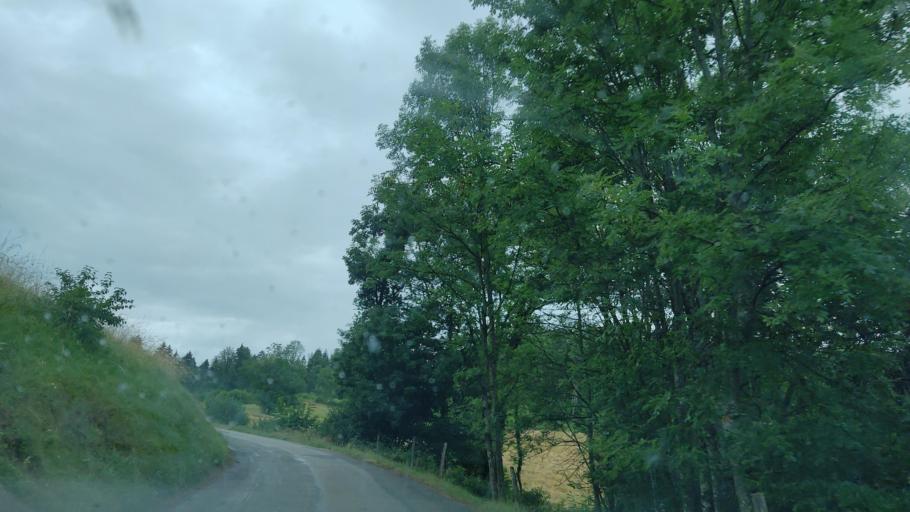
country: FR
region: Rhone-Alpes
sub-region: Departement de la Savoie
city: Coise-Saint-Jean-Pied-Gauthier
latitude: 45.5111
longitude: 6.1501
